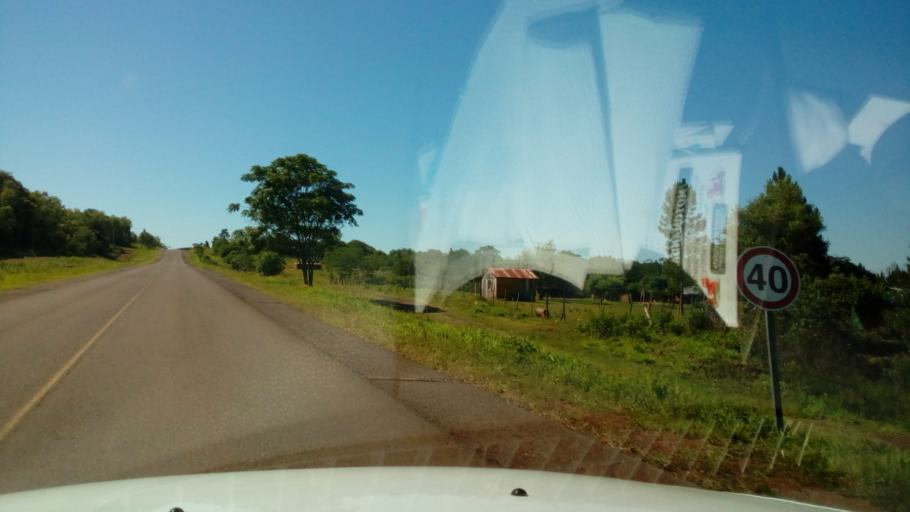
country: AR
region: Misiones
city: Almafuerte
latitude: -27.5450
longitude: -55.4318
